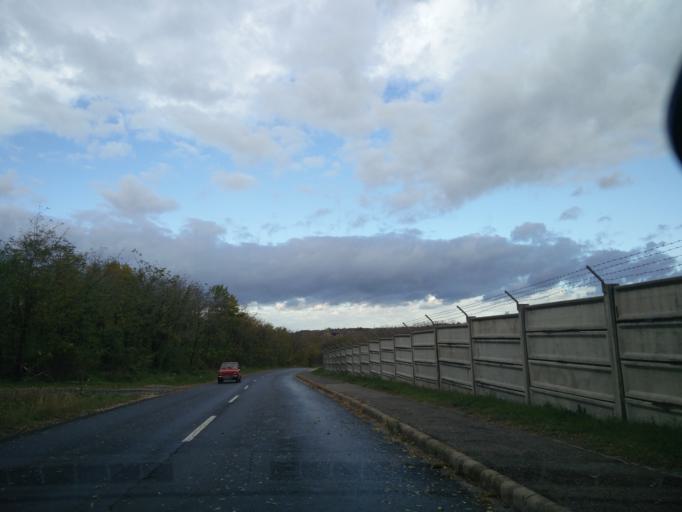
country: HU
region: Pest
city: Mogyorod
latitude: 47.5850
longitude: 19.2416
